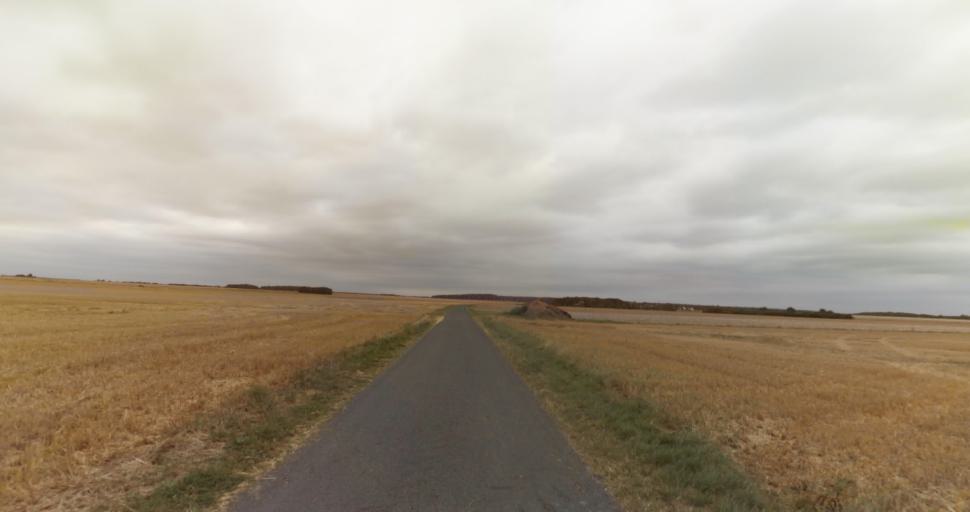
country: FR
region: Haute-Normandie
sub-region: Departement de l'Eure
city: La Couture-Boussey
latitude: 48.9415
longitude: 1.3371
